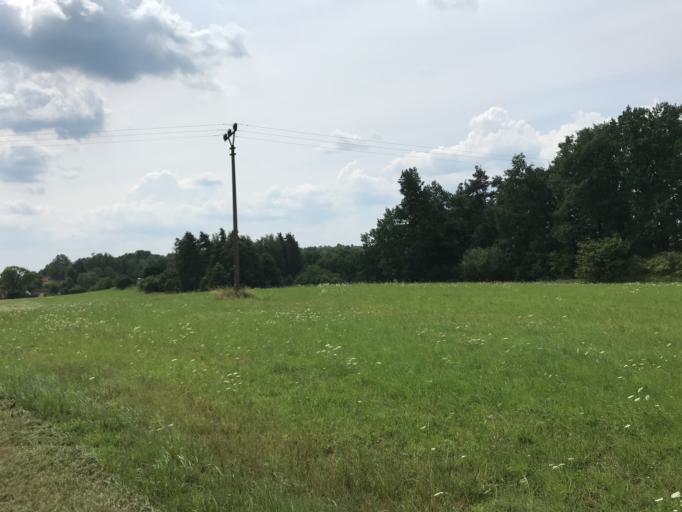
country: CZ
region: Jihocesky
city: Chlum u Trebone
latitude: 48.9701
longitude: 14.9245
